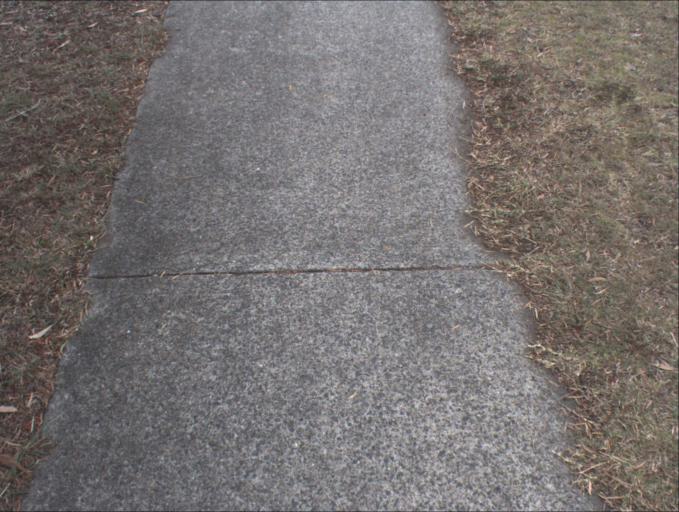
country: AU
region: Queensland
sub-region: Logan
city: Springwood
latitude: -27.6220
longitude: 153.1297
